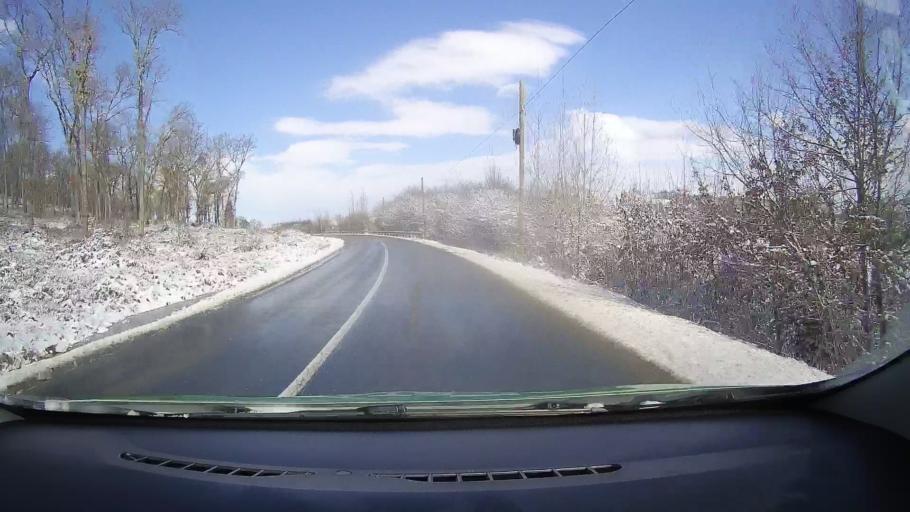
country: RO
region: Sibiu
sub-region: Comuna Nocrich
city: Nocrich
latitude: 45.8625
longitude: 24.4541
